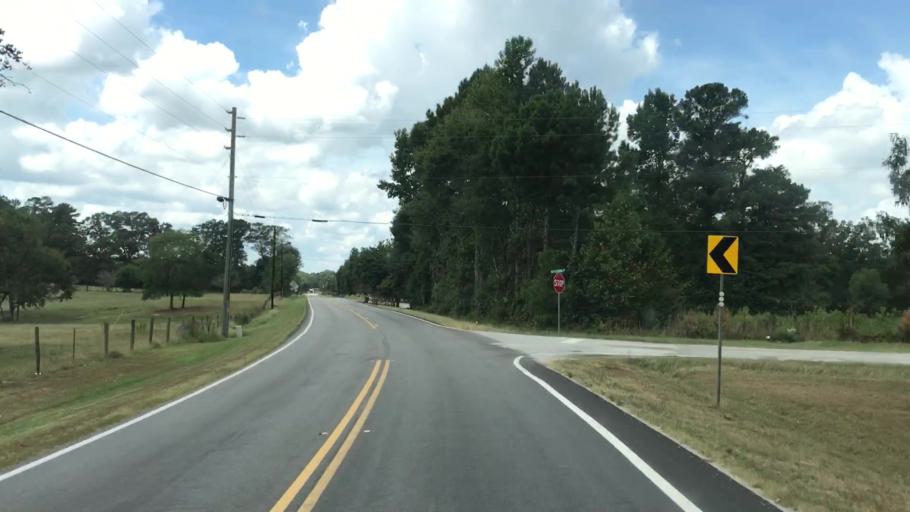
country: US
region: Georgia
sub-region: Greene County
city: Greensboro
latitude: 33.5606
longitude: -83.1226
